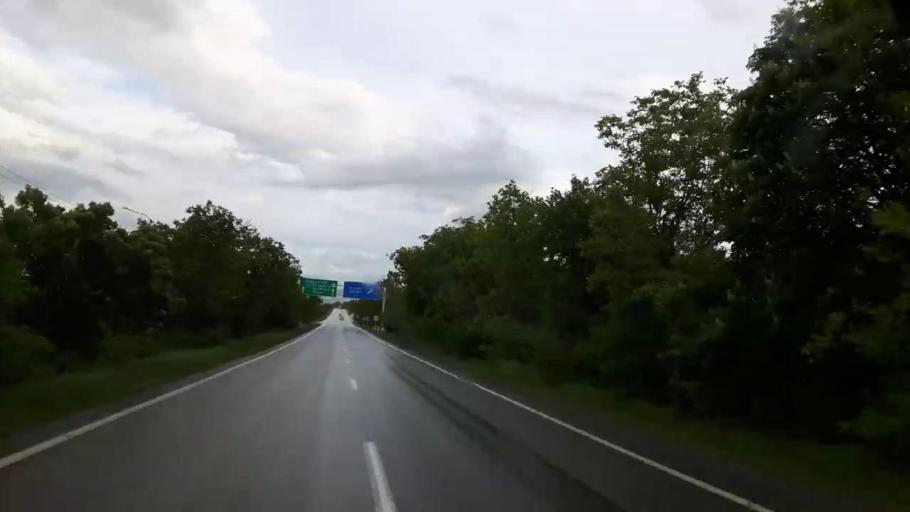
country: GE
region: Shida Kartli
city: Kaspi
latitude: 41.9658
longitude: 44.4655
